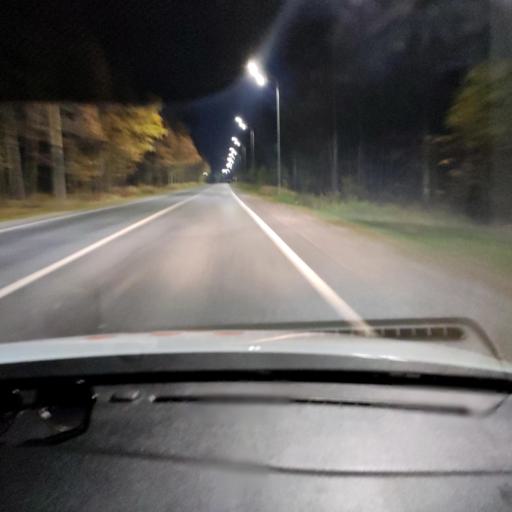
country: RU
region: Tatarstan
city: Stolbishchi
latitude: 55.6339
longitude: 49.0919
